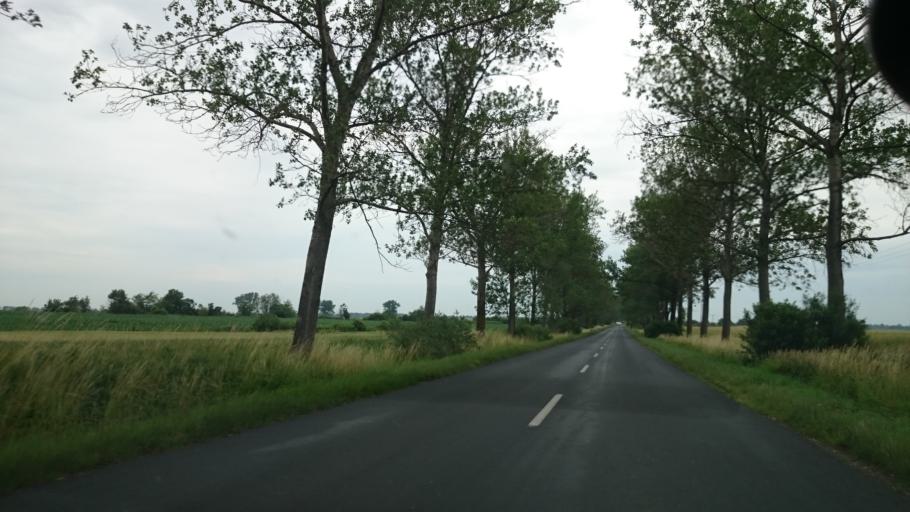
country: PL
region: Opole Voivodeship
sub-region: Powiat brzeski
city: Grodkow
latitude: 50.6811
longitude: 17.3403
